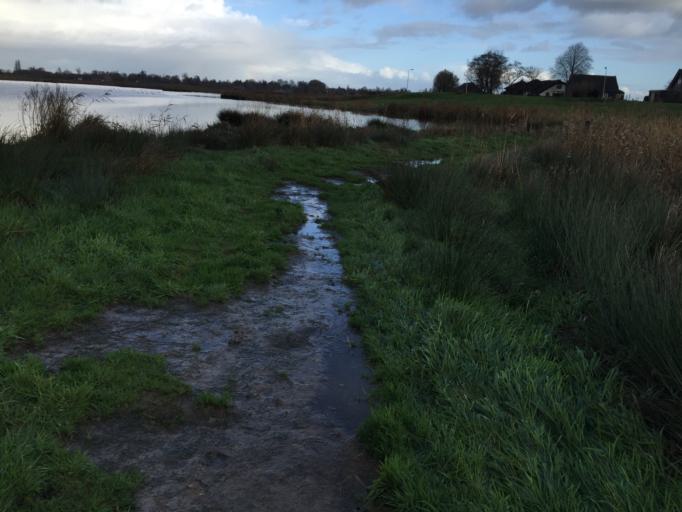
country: NL
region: Utrecht
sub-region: Gemeente De Ronde Venen
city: Mijdrecht
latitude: 52.1756
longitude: 4.8265
